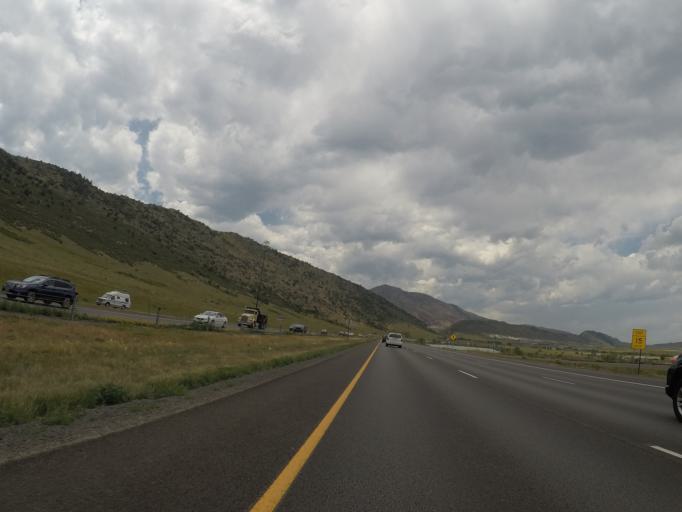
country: US
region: Colorado
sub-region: Jefferson County
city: Indian Hills
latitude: 39.6401
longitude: -105.1709
